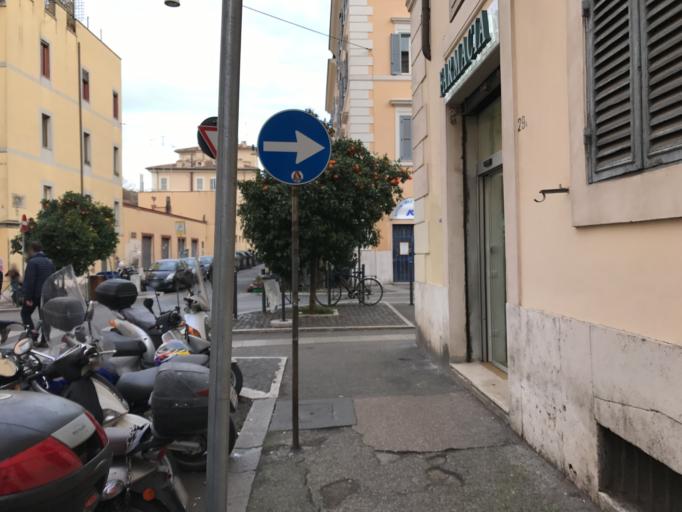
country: IT
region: Latium
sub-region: Citta metropolitana di Roma Capitale
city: Rome
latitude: 41.8891
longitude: 12.4964
